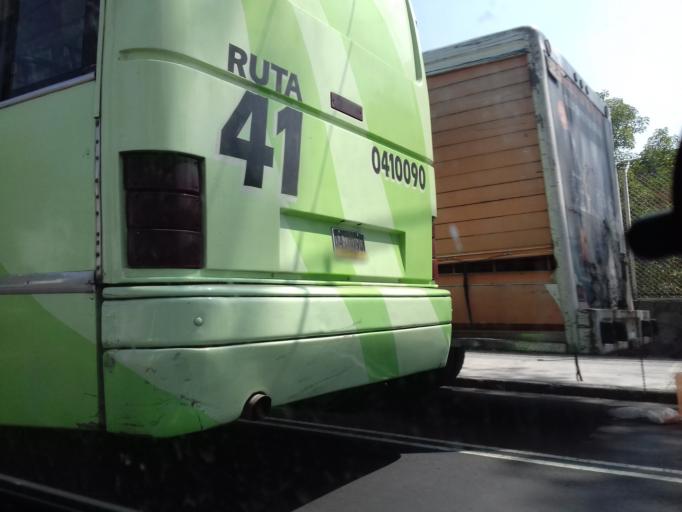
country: MX
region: Mexico City
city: Coyoacan
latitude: 19.3398
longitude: -99.1819
